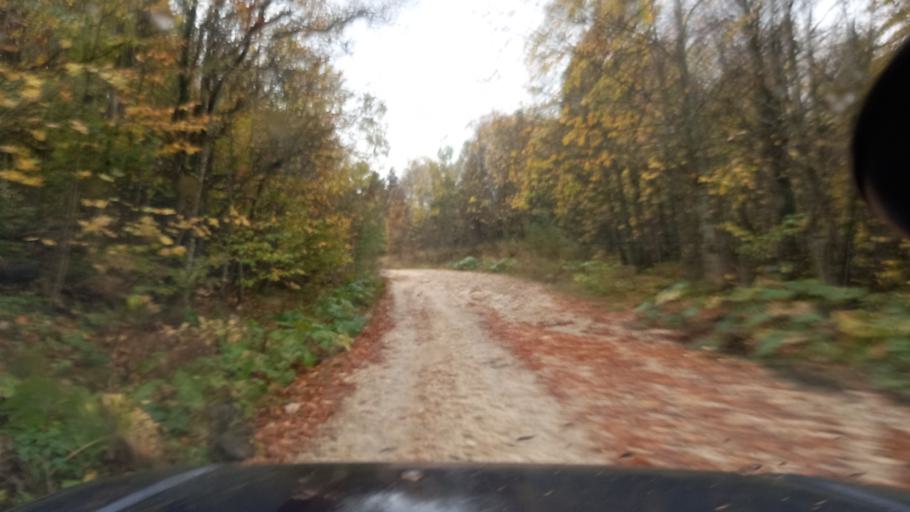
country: RU
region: Krasnodarskiy
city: Neftegorsk
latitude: 44.0249
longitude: 39.8385
